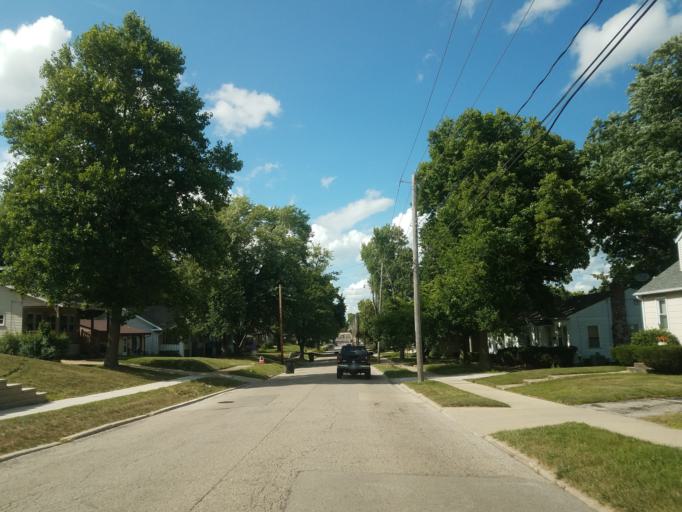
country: US
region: Illinois
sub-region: McLean County
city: Bloomington
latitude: 40.4902
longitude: -88.9818
